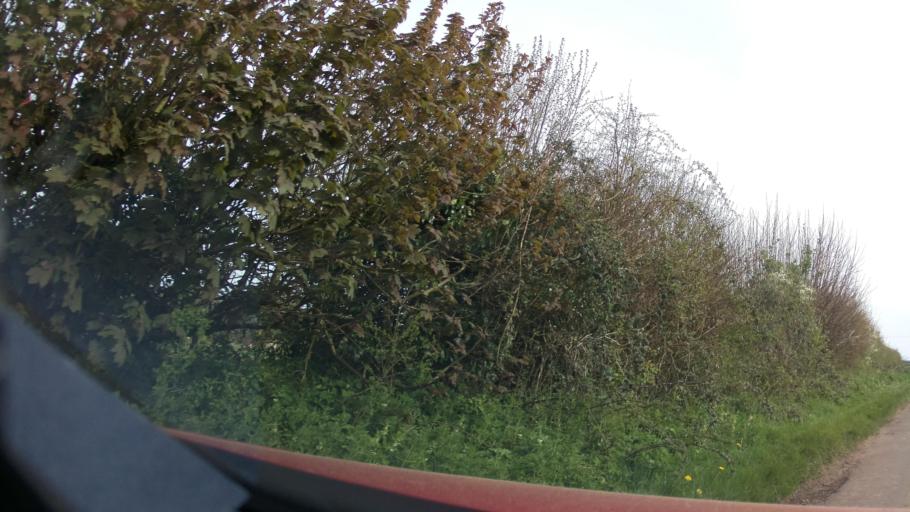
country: GB
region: England
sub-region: Somerset
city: Milborne Port
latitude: 50.9881
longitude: -2.4753
